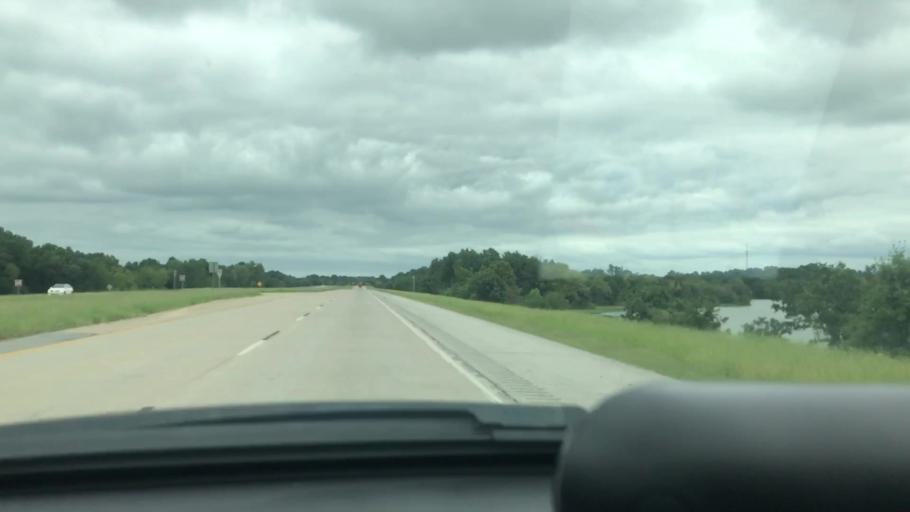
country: US
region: Oklahoma
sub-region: Wagoner County
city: Wagoner
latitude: 35.8995
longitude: -95.4026
